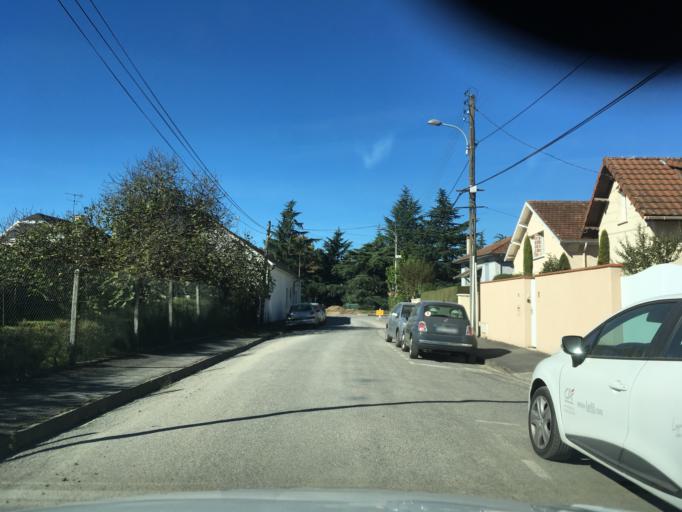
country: FR
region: Aquitaine
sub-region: Departement des Pyrenees-Atlantiques
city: Pau
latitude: 43.3141
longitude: -0.3606
